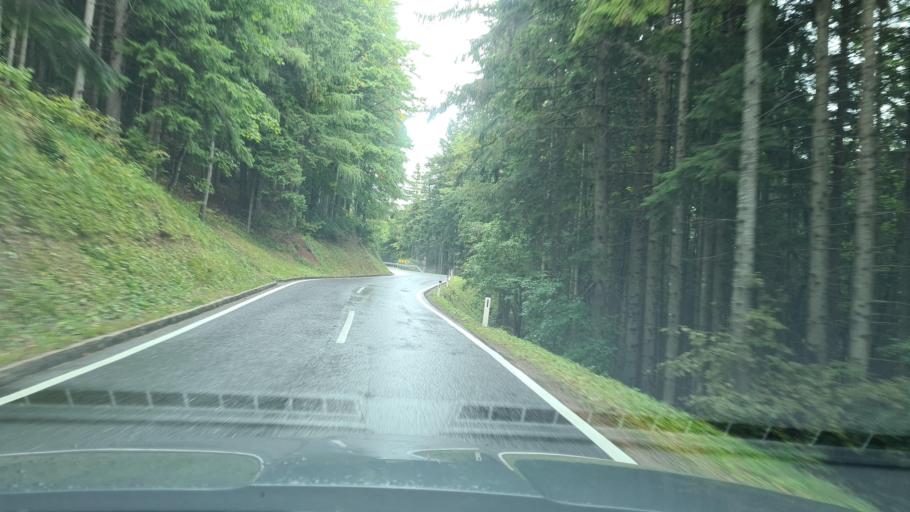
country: AT
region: Styria
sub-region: Politischer Bezirk Weiz
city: Passail
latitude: 47.3096
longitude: 15.4846
